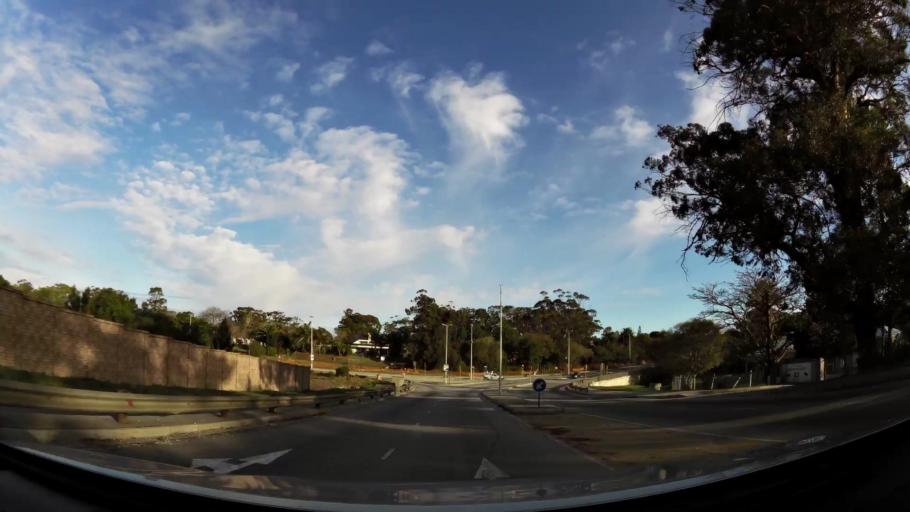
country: ZA
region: Eastern Cape
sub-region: Nelson Mandela Bay Metropolitan Municipality
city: Port Elizabeth
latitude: -33.9582
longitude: 25.5147
